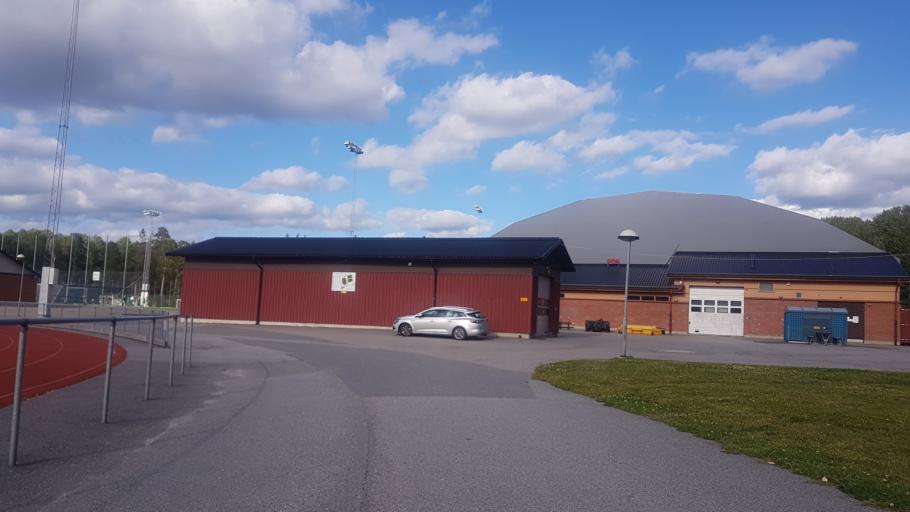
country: SE
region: Stockholm
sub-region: Nacka Kommun
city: Nacka
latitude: 59.2852
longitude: 18.1230
